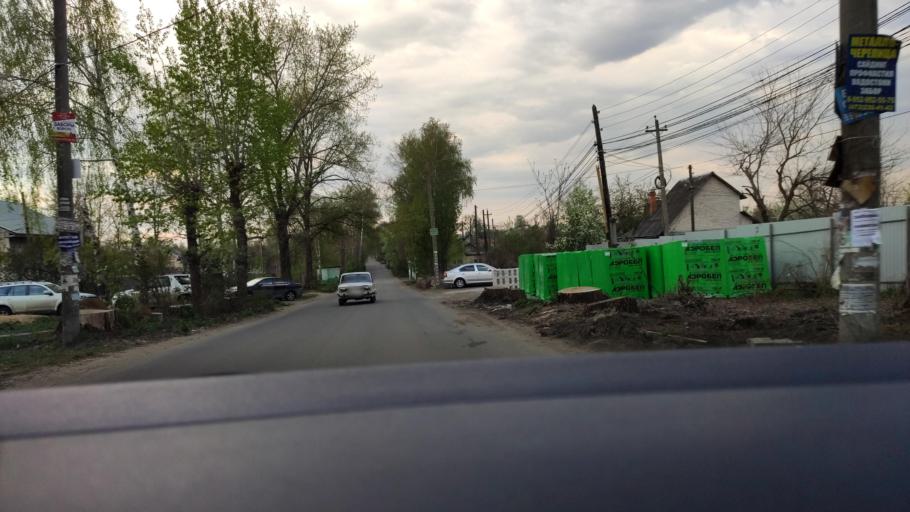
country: RU
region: Voronezj
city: Voronezh
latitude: 51.6037
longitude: 39.1589
